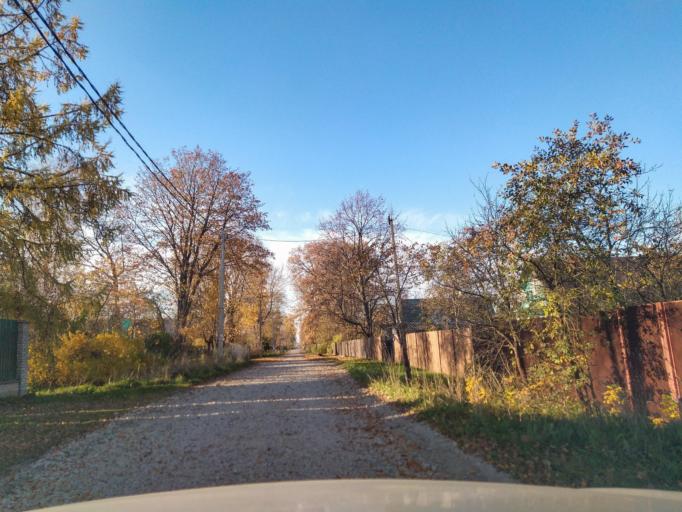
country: RU
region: Leningrad
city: Siverskiy
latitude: 59.3239
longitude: 30.0444
